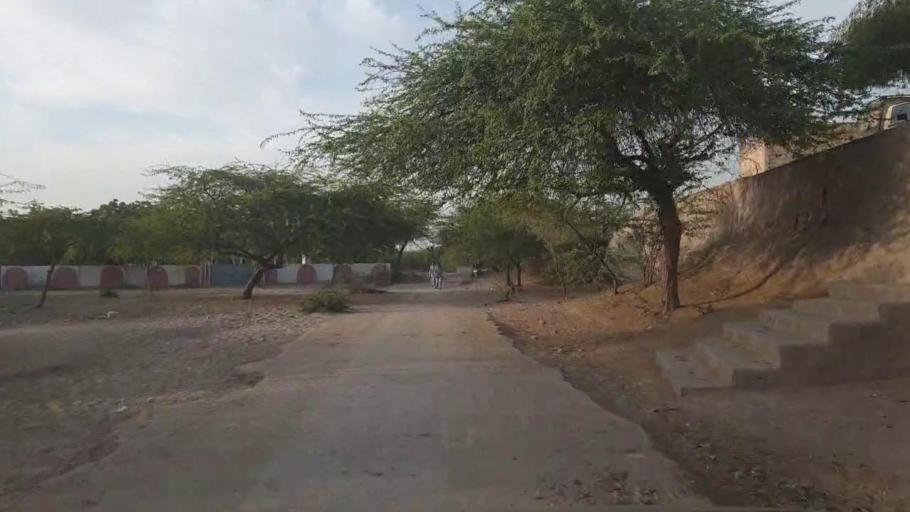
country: PK
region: Sindh
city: Nabisar
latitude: 25.1541
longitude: 69.6796
